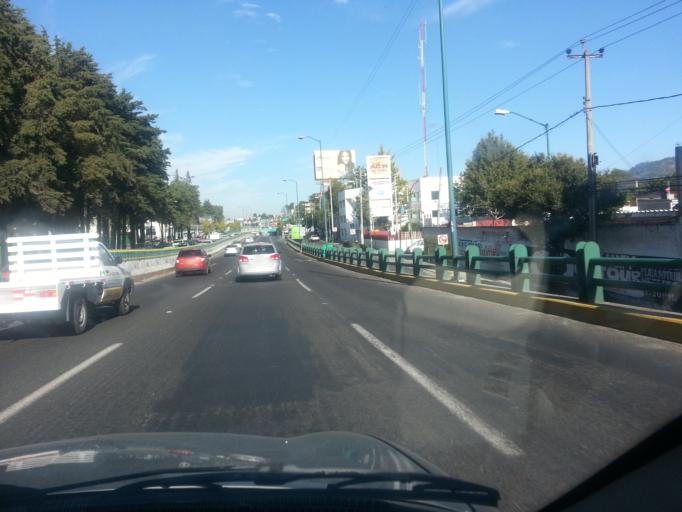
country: MX
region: Mexico
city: Toluca
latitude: 19.2726
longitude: -99.6549
